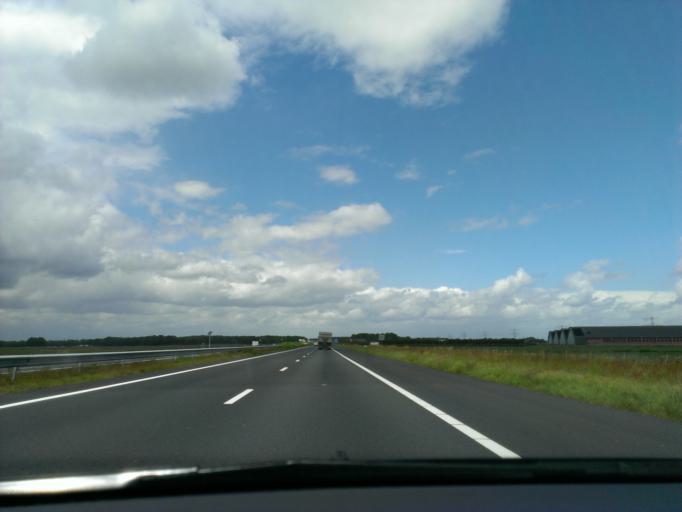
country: NL
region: Limburg
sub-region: Gemeente Venray
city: Venray
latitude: 51.4944
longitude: 6.0355
